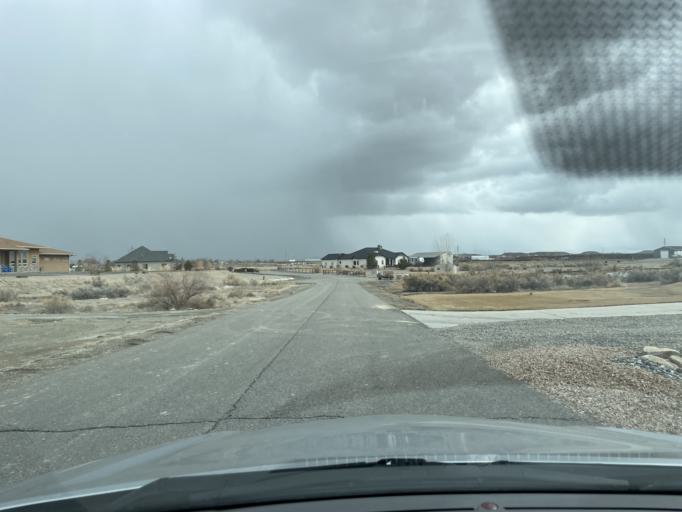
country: US
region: Colorado
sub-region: Mesa County
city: Loma
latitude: 39.2176
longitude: -108.8076
